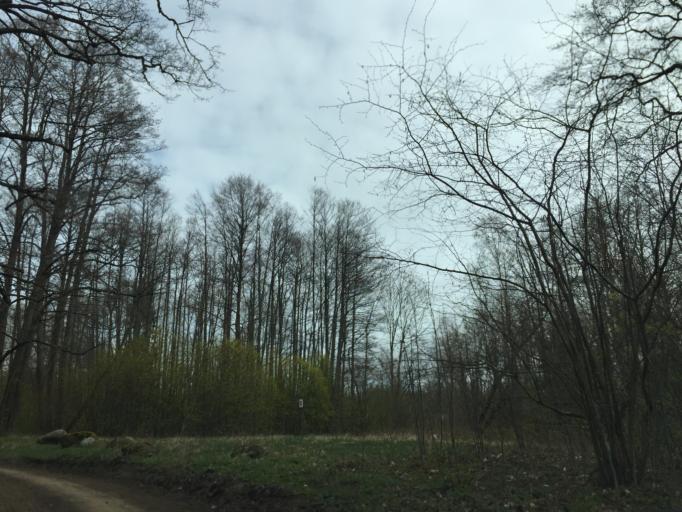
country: LV
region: Salacgrivas
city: Salacgriva
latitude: 57.5213
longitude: 24.3793
